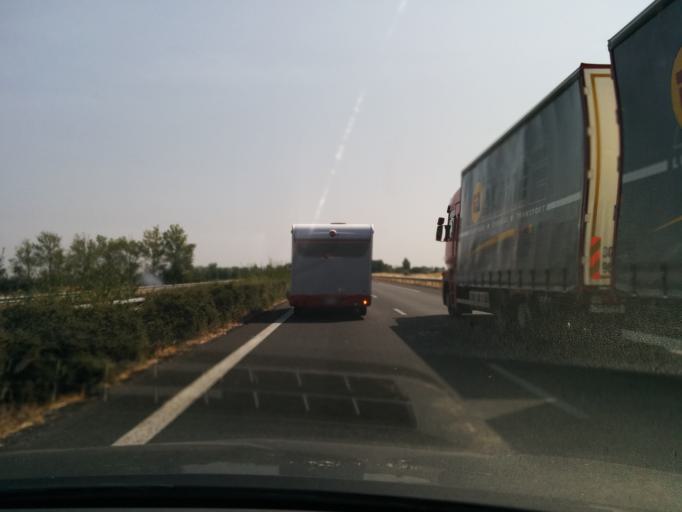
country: FR
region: Midi-Pyrenees
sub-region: Departement du Tarn
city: Brens
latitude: 43.8866
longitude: 1.9463
